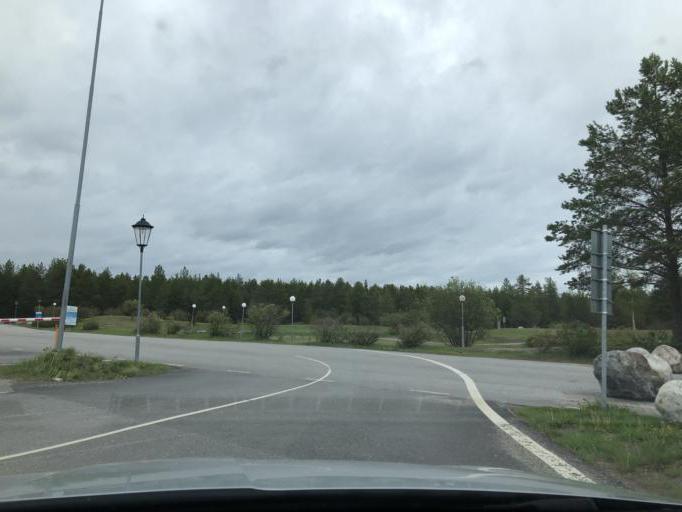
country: SE
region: Norrbotten
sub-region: Pitea Kommun
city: Pitea
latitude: 65.2352
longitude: 21.5306
